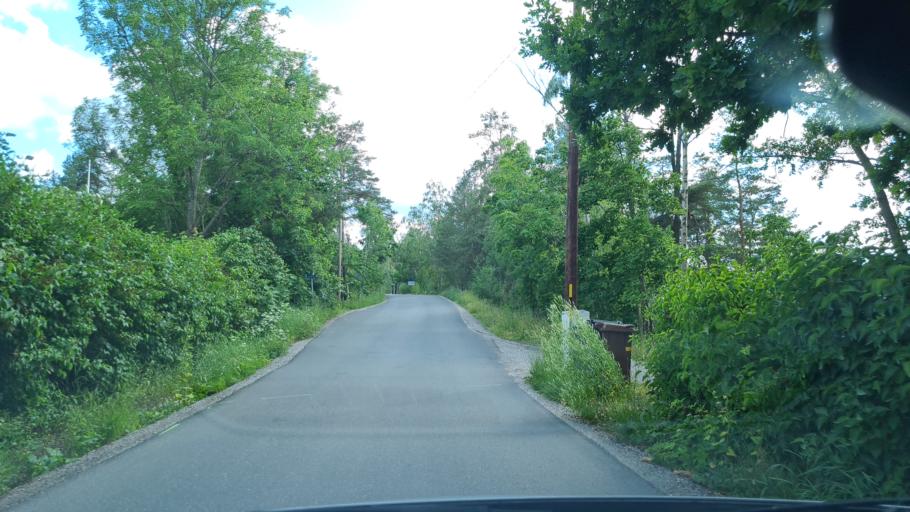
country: SE
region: Stockholm
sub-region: Vaxholms Kommun
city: Vaxholm
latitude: 59.4093
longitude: 18.3703
